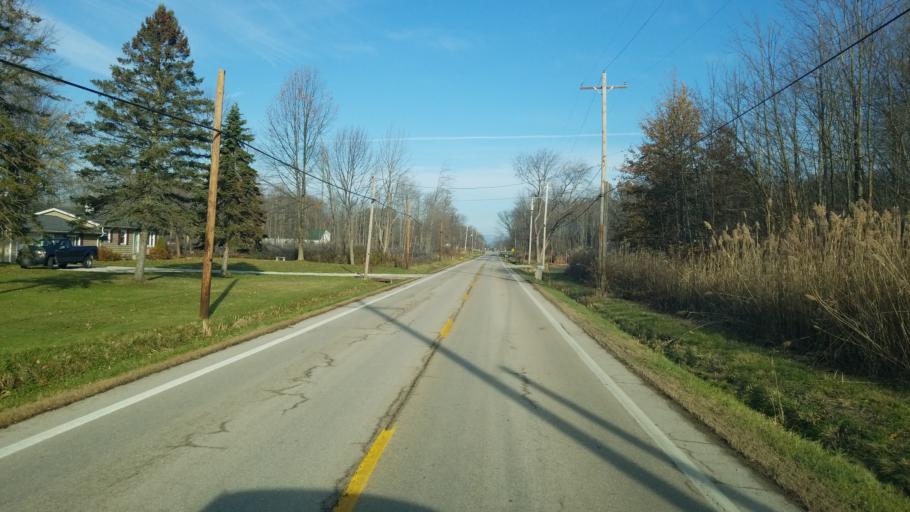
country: US
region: Ohio
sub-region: Ashtabula County
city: North Kingsville
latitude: 41.9137
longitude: -80.6938
